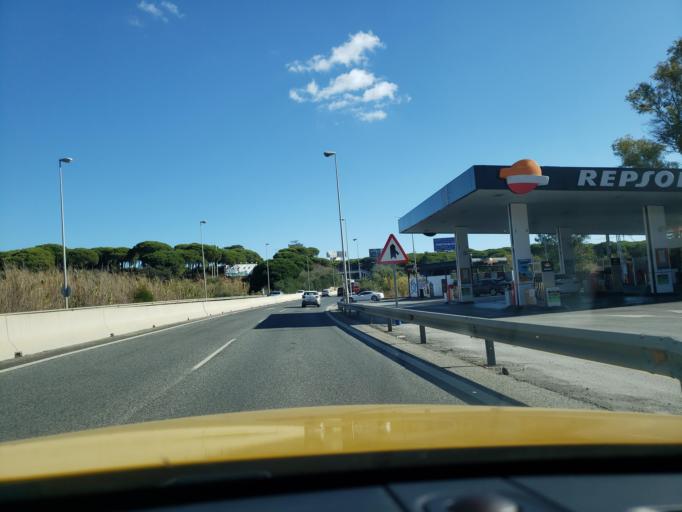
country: ES
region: Andalusia
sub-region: Provincia de Malaga
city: Ojen
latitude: 36.4938
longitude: -4.7647
